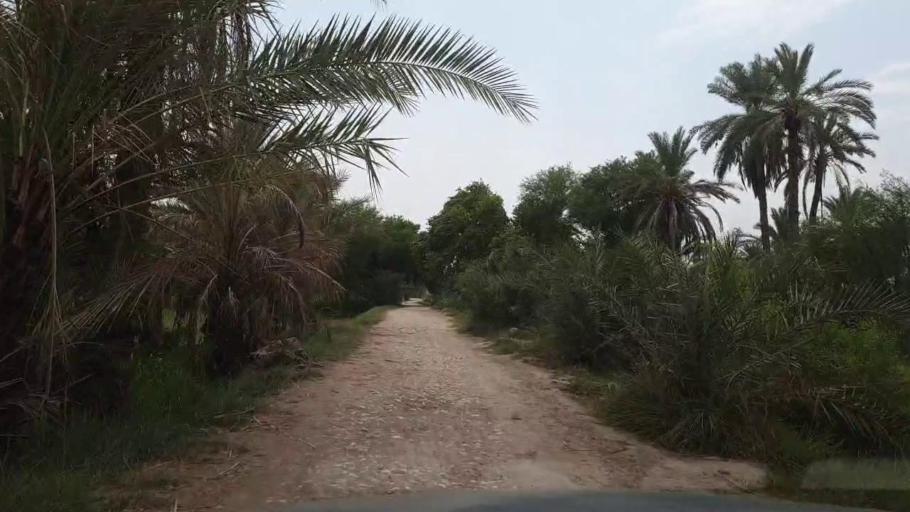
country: PK
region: Sindh
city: Pir jo Goth
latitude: 27.4897
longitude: 68.5953
